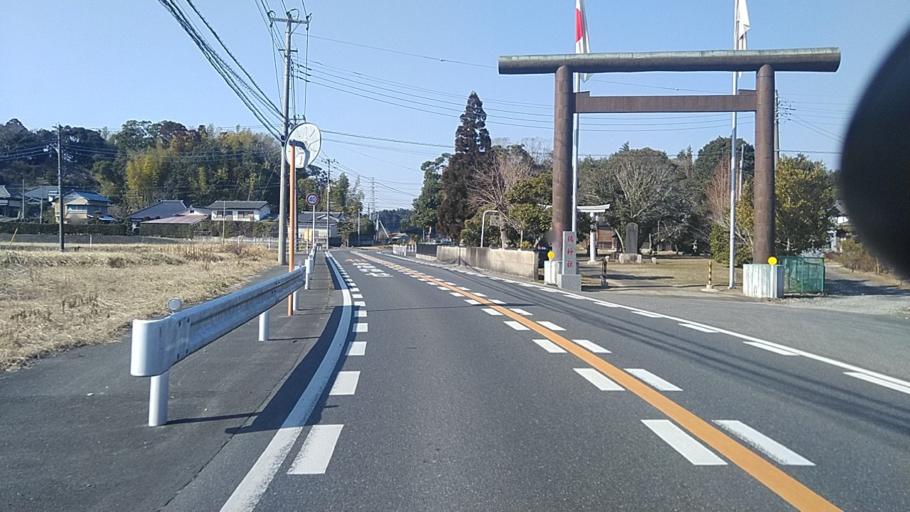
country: JP
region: Chiba
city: Mobara
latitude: 35.4608
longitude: 140.2851
